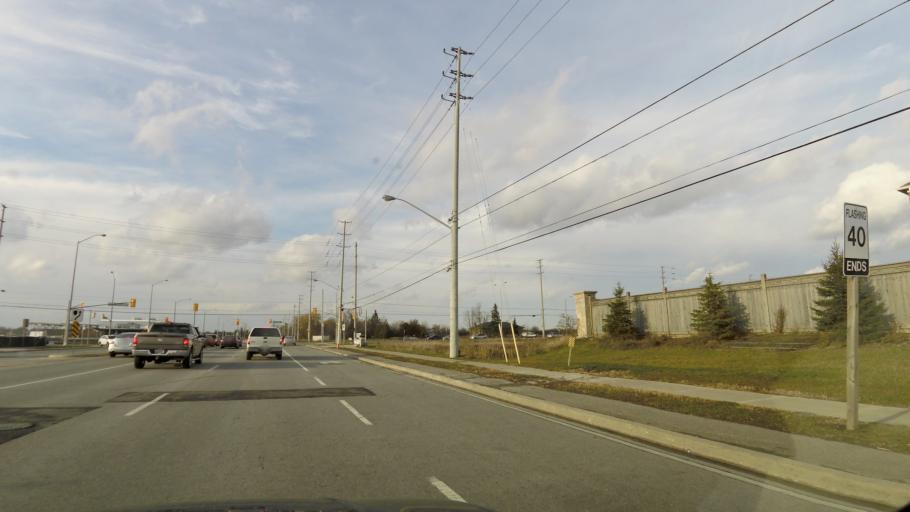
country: CA
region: Ontario
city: Brampton
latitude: 43.7914
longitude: -79.6889
